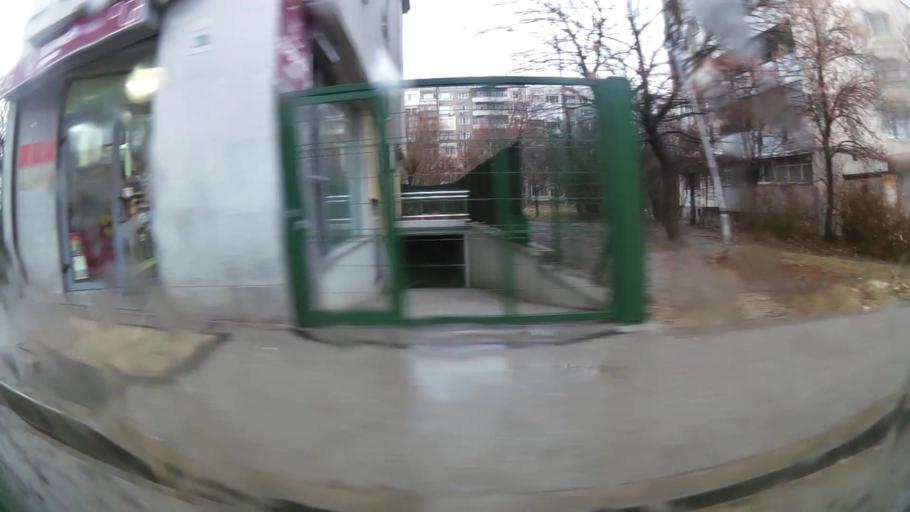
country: BG
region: Sofia-Capital
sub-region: Stolichna Obshtina
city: Sofia
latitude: 42.6595
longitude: 23.3654
